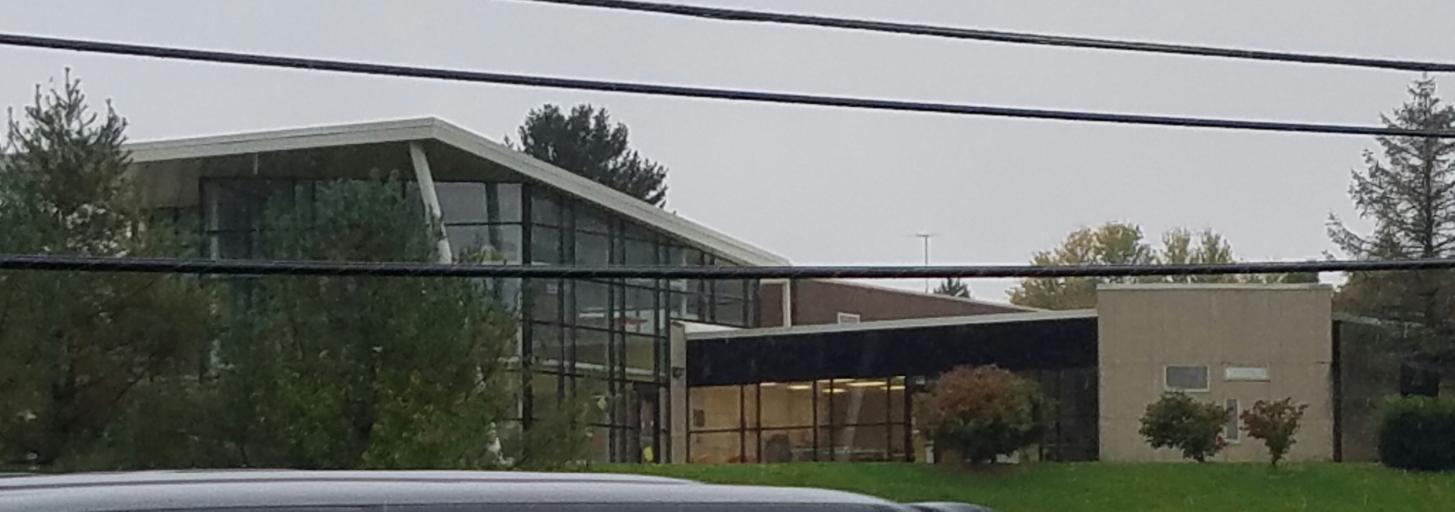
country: US
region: Ohio
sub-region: Morrow County
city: Mount Gilead
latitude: 40.5545
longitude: -82.8202
